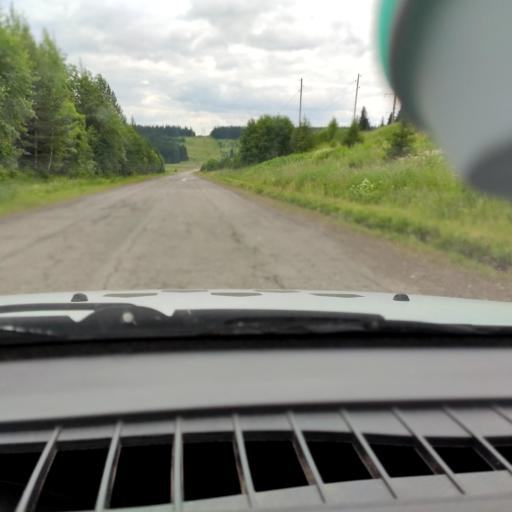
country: RU
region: Perm
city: Uinskoye
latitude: 57.1223
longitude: 56.5534
